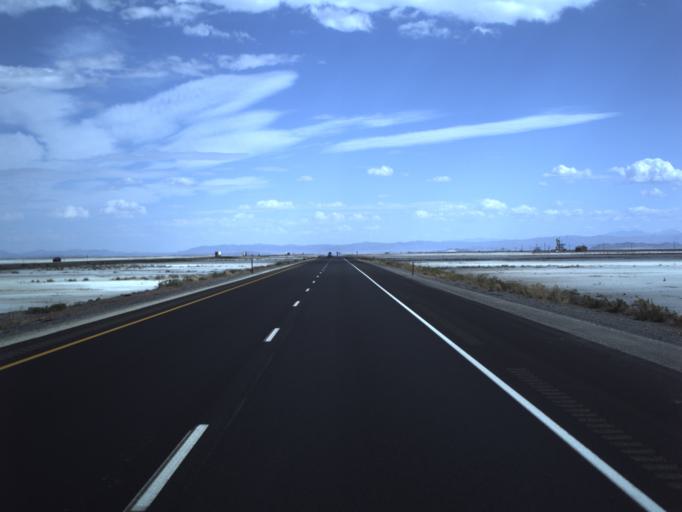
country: US
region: Utah
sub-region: Tooele County
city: Wendover
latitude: 40.7308
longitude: -113.4979
